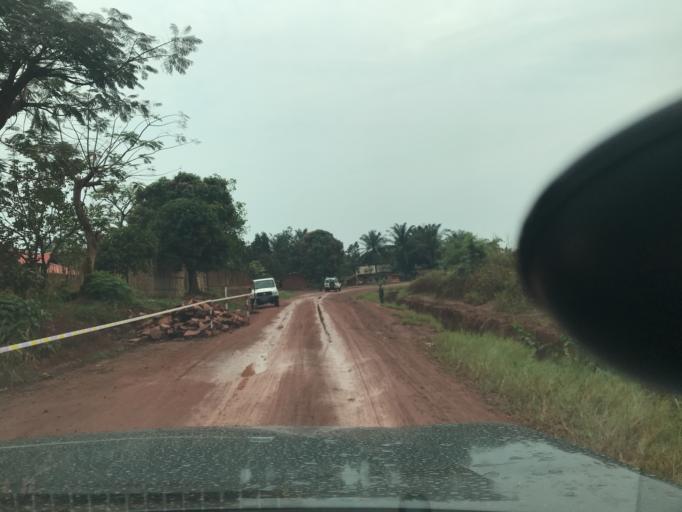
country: CD
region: Equateur
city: Gemena
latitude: 3.2346
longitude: 19.7810
